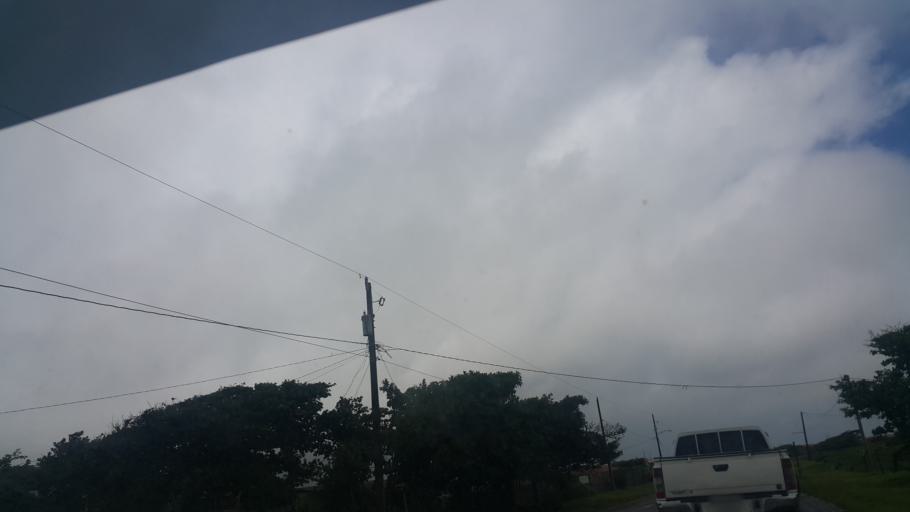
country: NI
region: Managua
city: El Crucero
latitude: 11.9495
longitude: -86.3007
